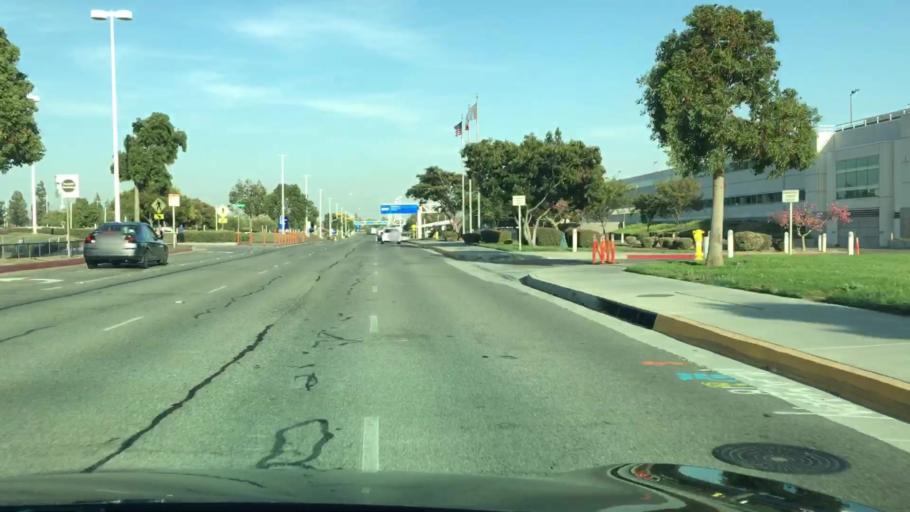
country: US
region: California
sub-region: San Bernardino County
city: Rancho Cucamonga
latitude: 34.0608
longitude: -117.5905
